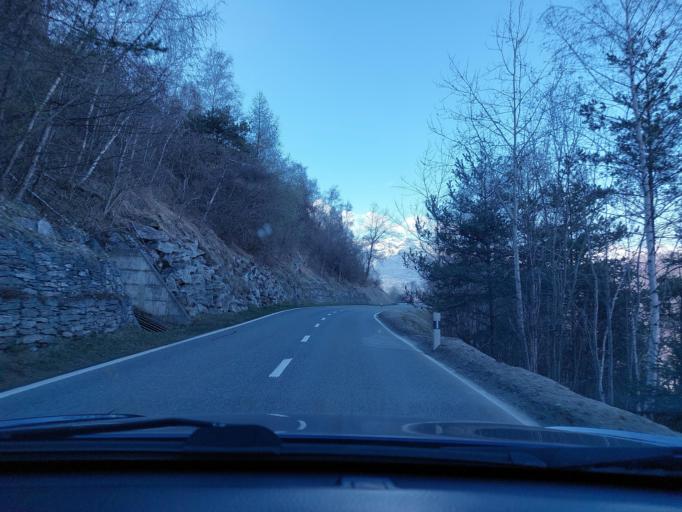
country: CH
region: Valais
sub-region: Herens District
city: Heremence
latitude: 46.1912
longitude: 7.4081
